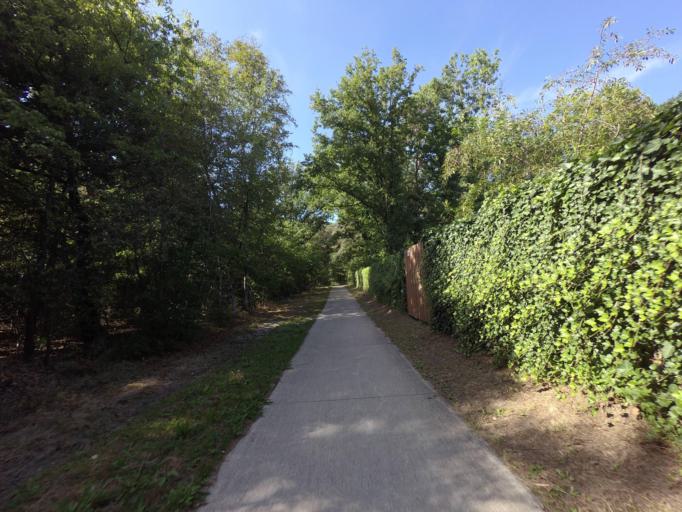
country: NL
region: Gelderland
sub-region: Gemeente Apeldoorn
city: Loenen
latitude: 52.1481
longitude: 6.0281
